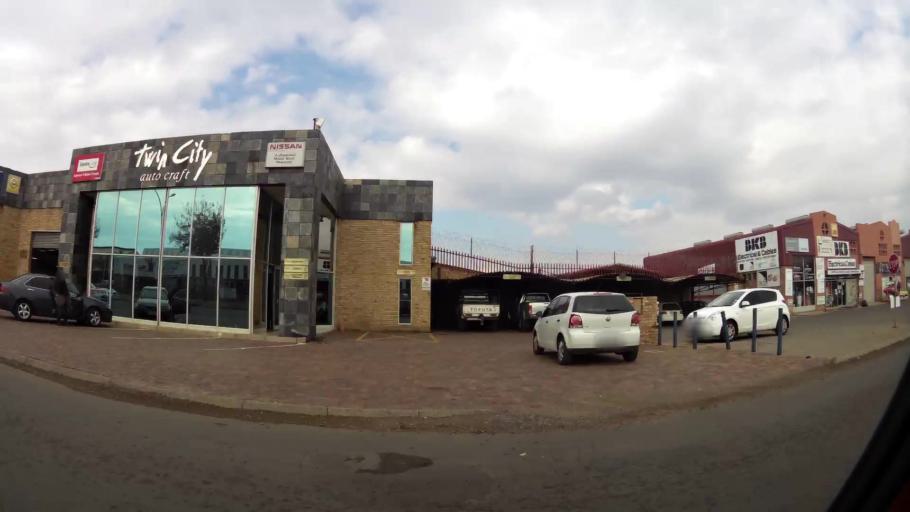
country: ZA
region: Gauteng
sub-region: Sedibeng District Municipality
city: Vanderbijlpark
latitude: -26.7056
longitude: 27.8508
